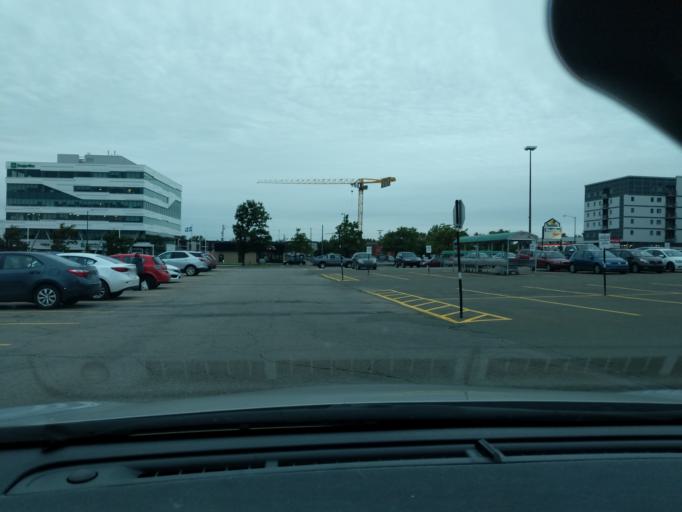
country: CA
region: Quebec
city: L'Ancienne-Lorette
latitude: 46.7646
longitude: -71.3101
